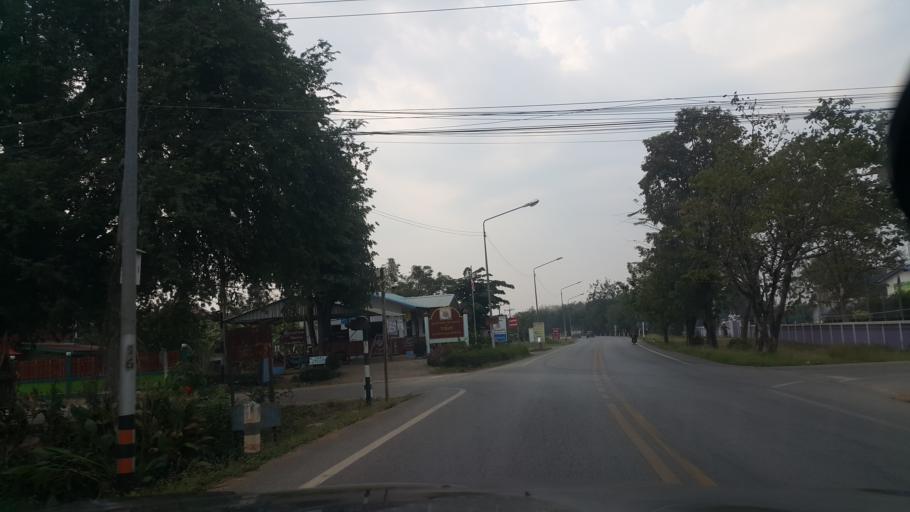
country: TH
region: Sukhothai
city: Si Samrong
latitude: 17.1149
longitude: 99.8901
